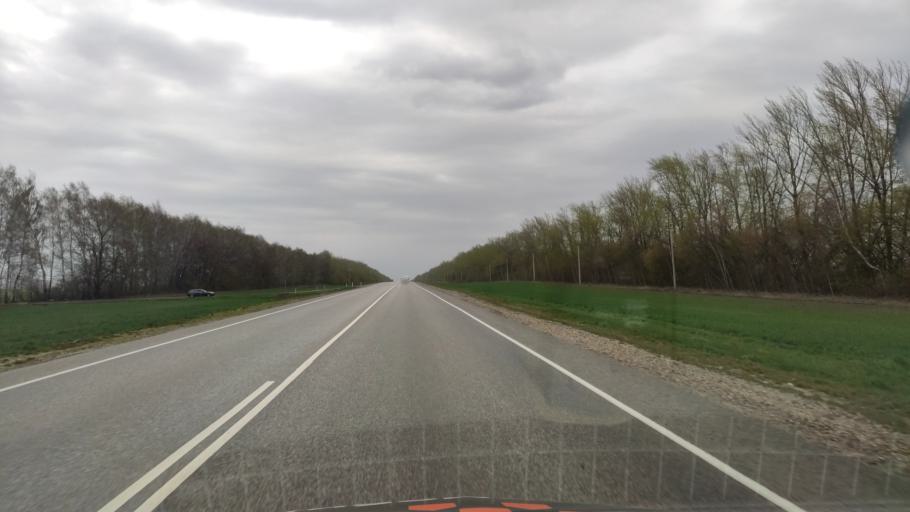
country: RU
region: Kursk
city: Gorshechnoye
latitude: 51.5494
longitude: 38.1538
